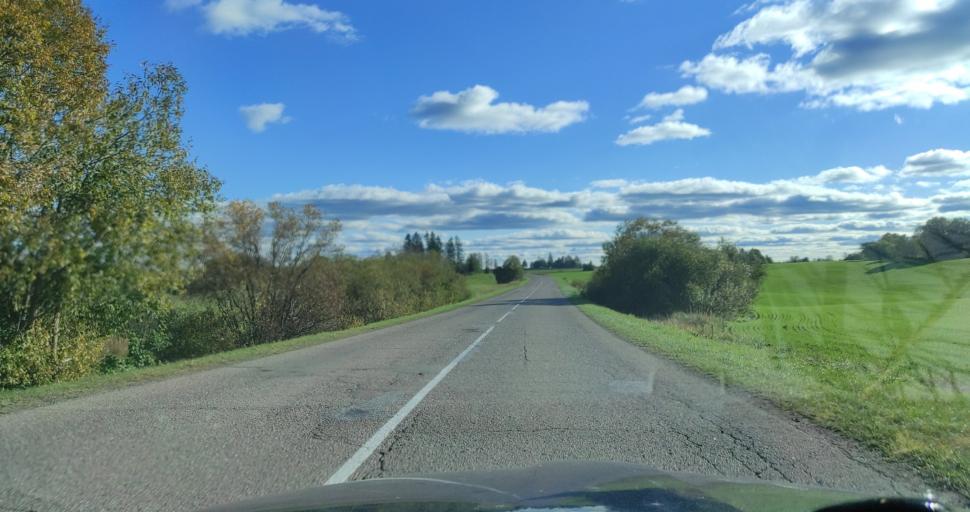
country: LV
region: Aizpute
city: Aizpute
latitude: 56.7626
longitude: 21.5416
